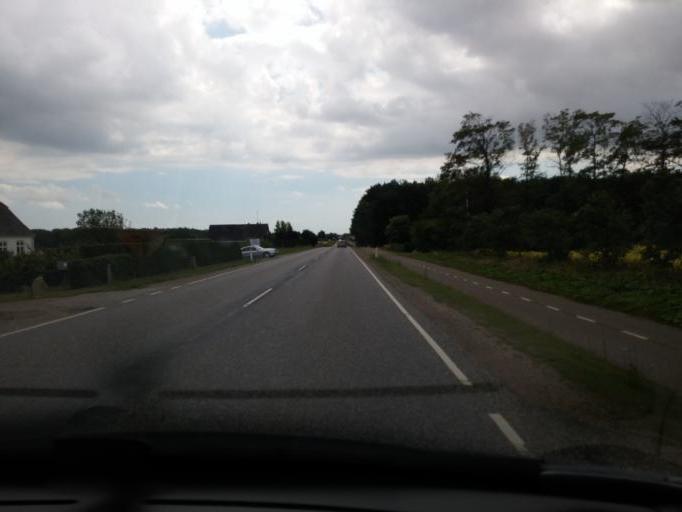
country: DK
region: South Denmark
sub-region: Svendborg Kommune
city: Vindeby
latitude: 55.0128
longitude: 10.6081
